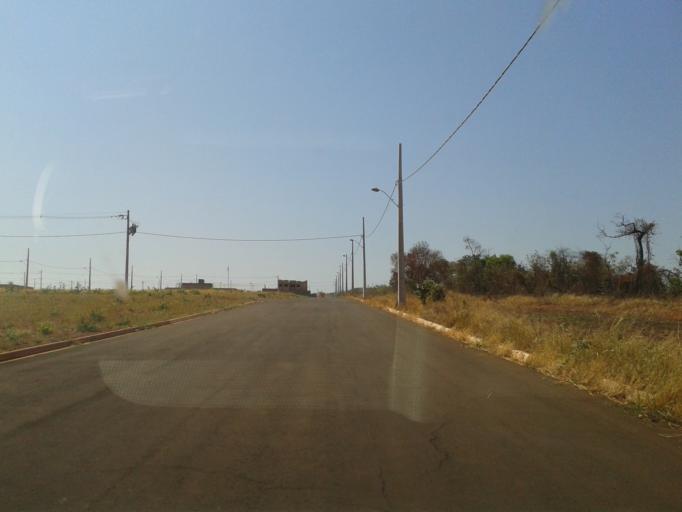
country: BR
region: Minas Gerais
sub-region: Ituiutaba
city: Ituiutaba
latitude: -19.0157
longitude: -49.4621
